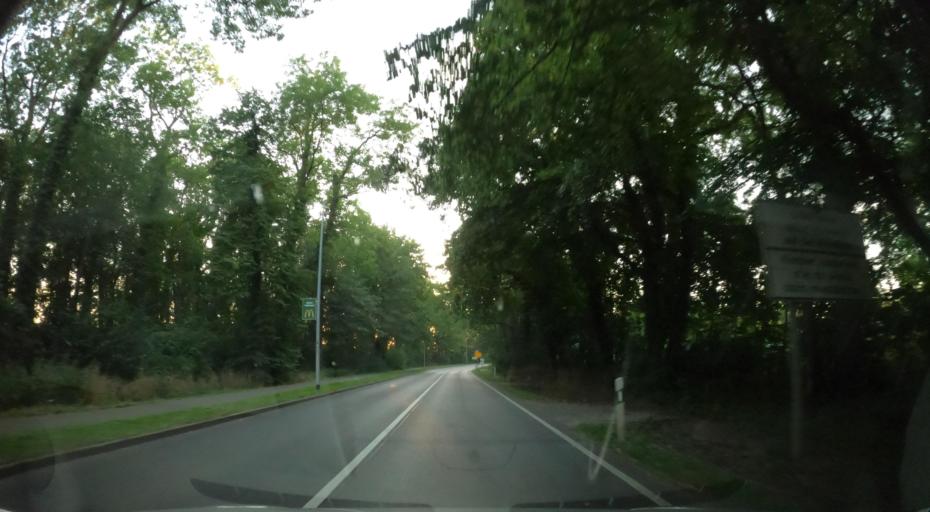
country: DE
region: Mecklenburg-Vorpommern
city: Strasburg
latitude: 53.5026
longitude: 13.7558
